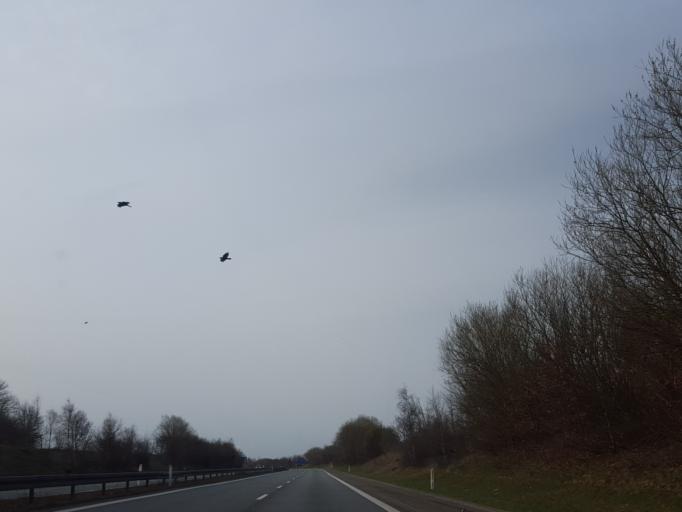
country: DK
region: South Denmark
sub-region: Esbjerg Kommune
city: Esbjerg
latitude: 55.4969
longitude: 8.5024
